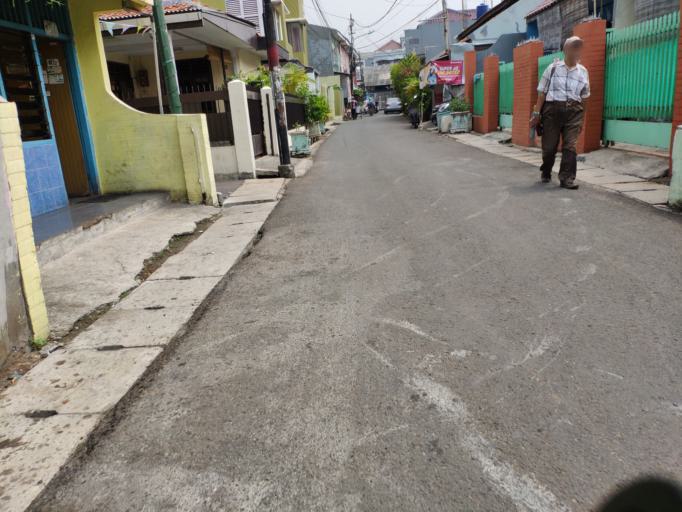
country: ID
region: Jakarta Raya
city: Jakarta
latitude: -6.1941
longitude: 106.8646
